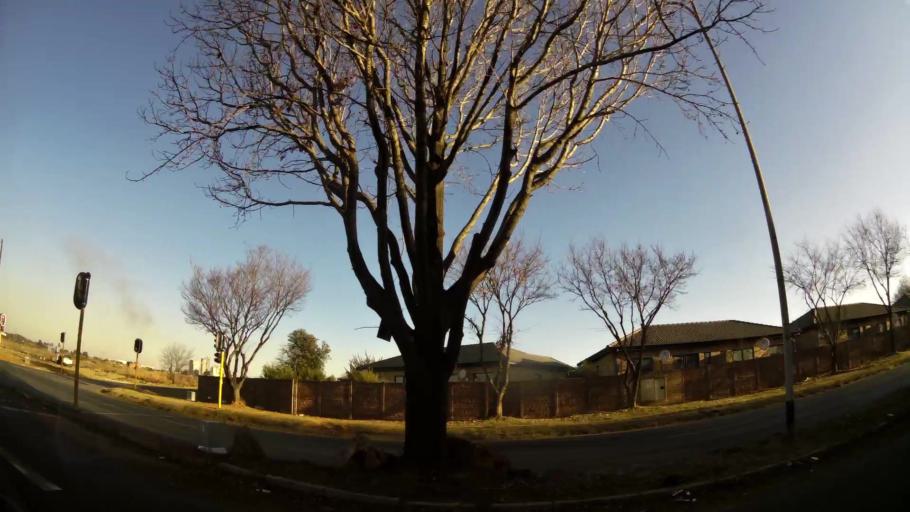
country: ZA
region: Gauteng
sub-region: City of Johannesburg Metropolitan Municipality
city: Roodepoort
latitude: -26.1706
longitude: 27.8829
